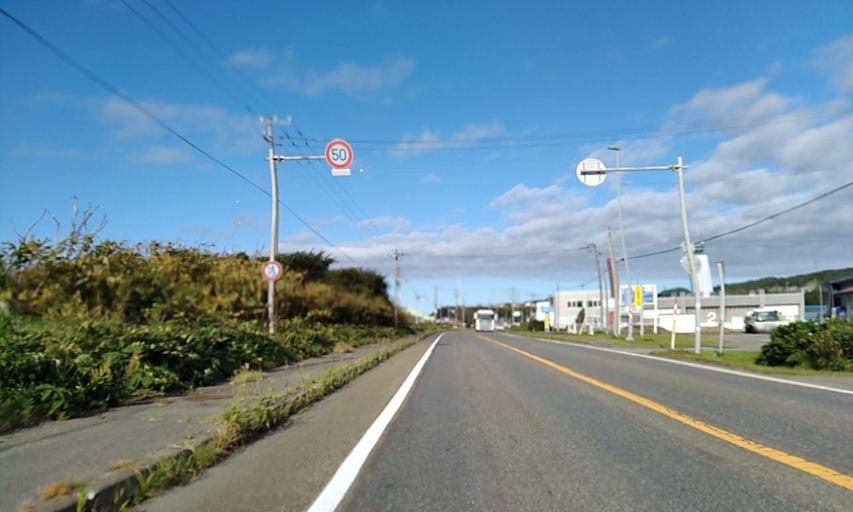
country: JP
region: Hokkaido
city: Shizunai-furukawacho
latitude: 42.2449
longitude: 142.5814
